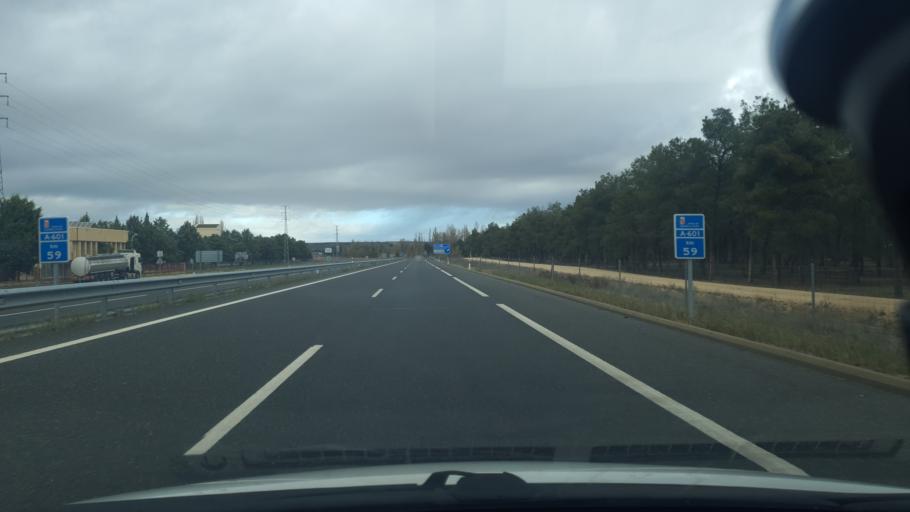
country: ES
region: Castille and Leon
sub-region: Provincia de Segovia
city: Sanchonuno
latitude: 41.3591
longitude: -4.2989
